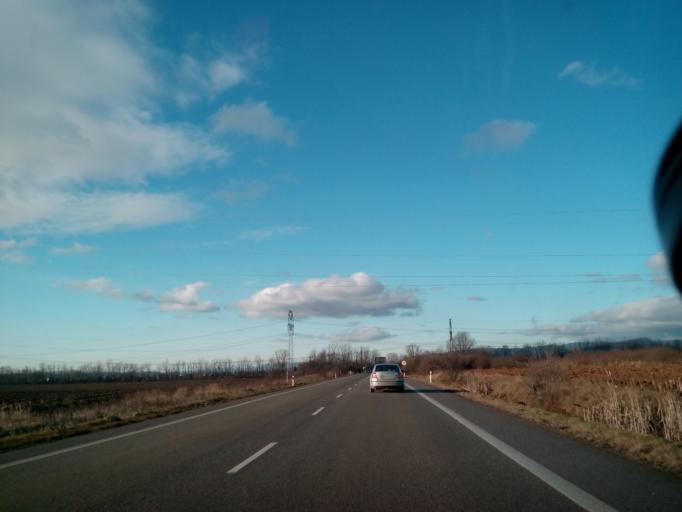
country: SK
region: Kosicky
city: Moldava nad Bodvou
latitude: 48.5979
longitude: 21.0496
